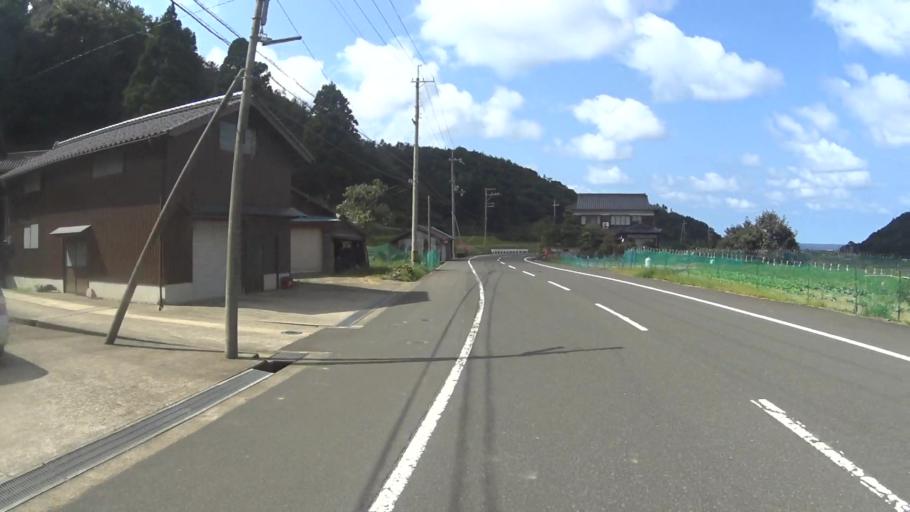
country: JP
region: Kyoto
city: Miyazu
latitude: 35.7469
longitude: 135.1784
